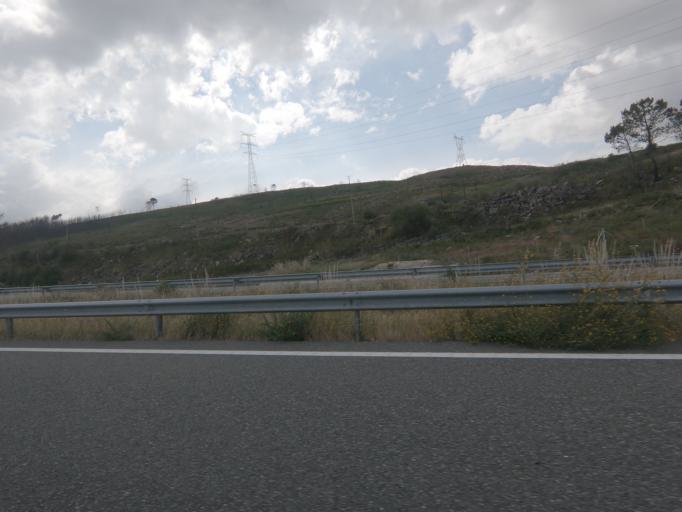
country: ES
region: Galicia
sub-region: Provincia de Ourense
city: Melon
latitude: 42.2641
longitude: -8.2113
